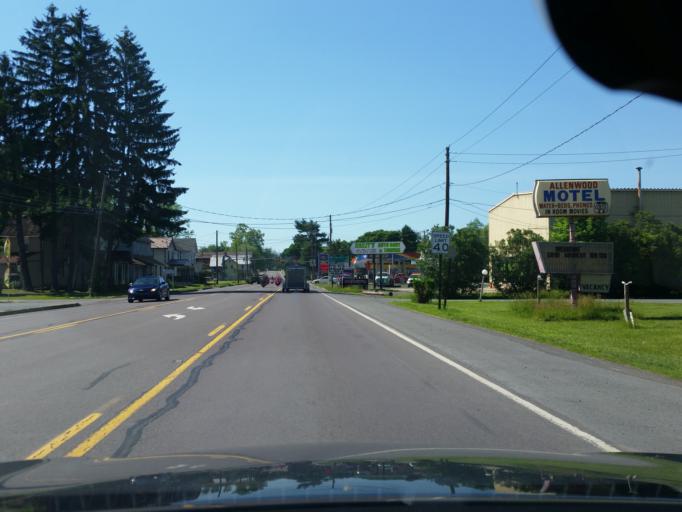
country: US
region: Pennsylvania
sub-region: Northumberland County
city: Dewart
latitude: 41.1063
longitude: -76.8970
